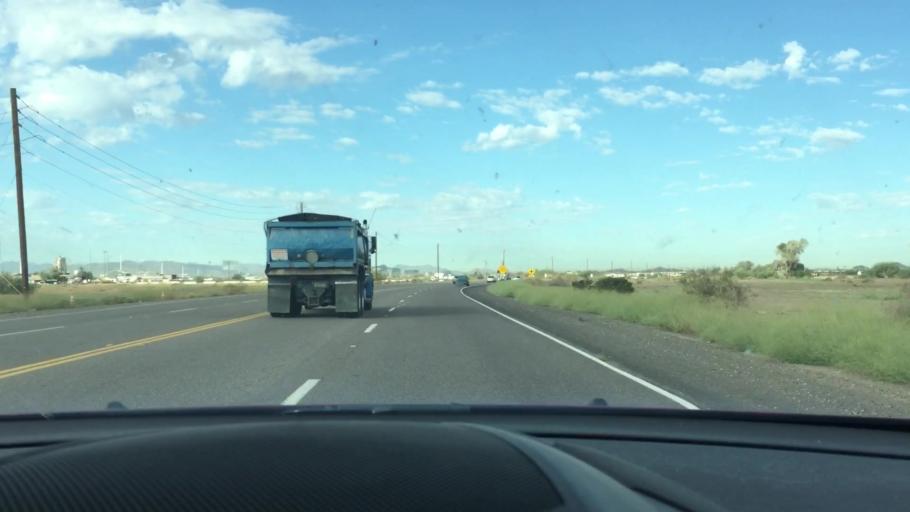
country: US
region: Arizona
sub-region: Maricopa County
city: Tempe
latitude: 33.4516
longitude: -111.8704
